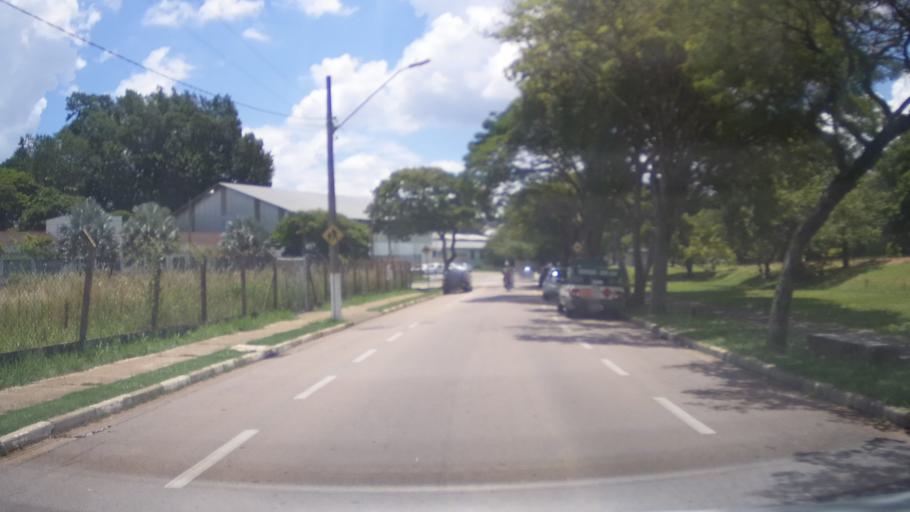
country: BR
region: Sao Paulo
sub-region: Vinhedo
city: Vinhedo
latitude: -23.0260
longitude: -46.9783
